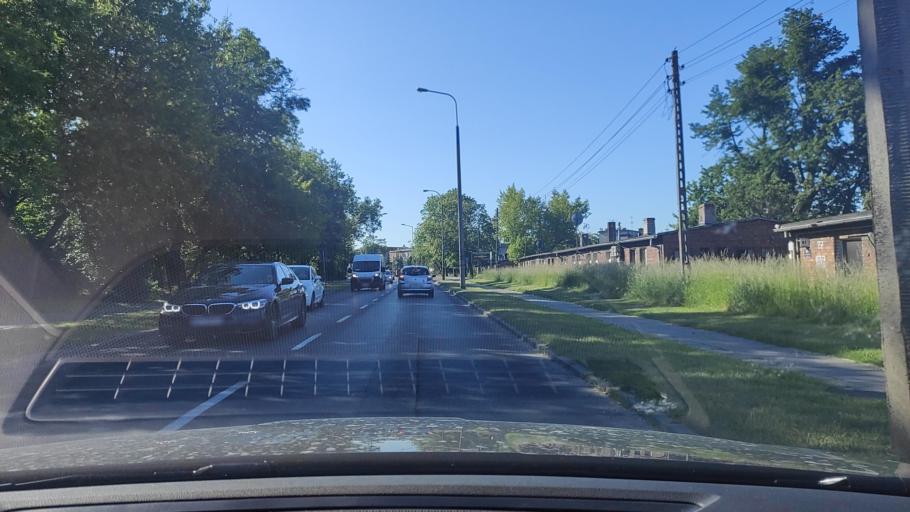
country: PL
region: Greater Poland Voivodeship
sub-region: Powiat poznanski
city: Lubon
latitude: 52.3732
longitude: 16.8947
